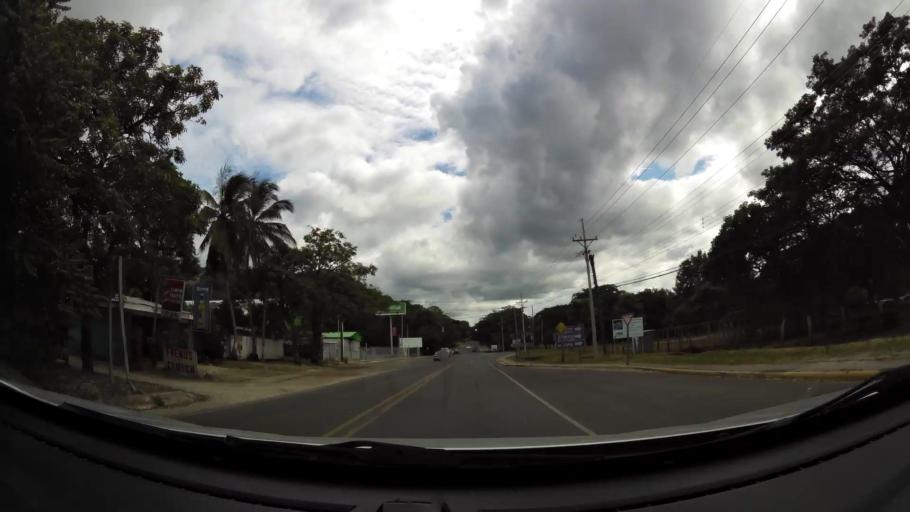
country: CR
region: Guanacaste
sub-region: Canton de Nicoya
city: Nicoya
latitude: 10.1614
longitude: -85.4495
